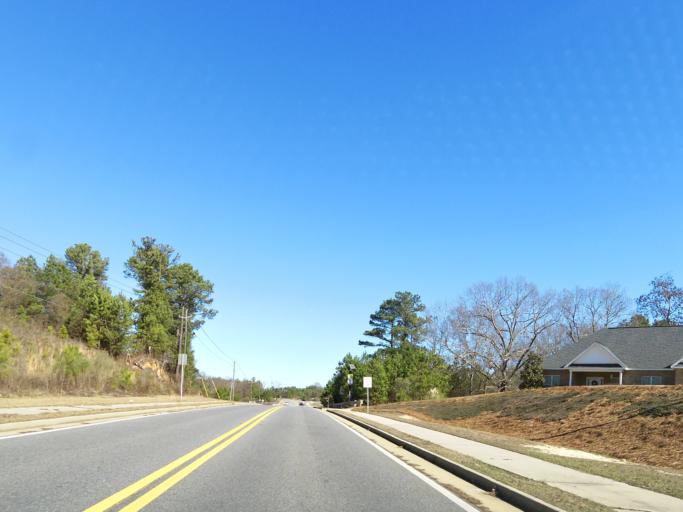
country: US
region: Georgia
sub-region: Peach County
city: Byron
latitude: 32.7363
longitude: -83.7192
